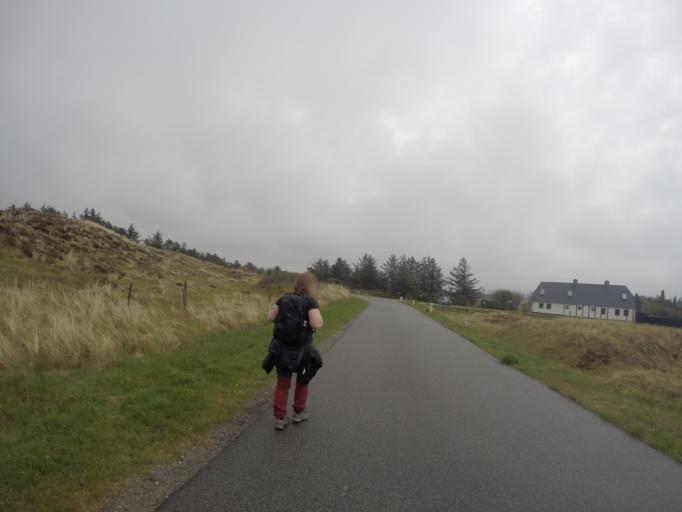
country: DK
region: North Denmark
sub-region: Thisted Kommune
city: Hanstholm
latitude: 57.0370
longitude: 8.5218
